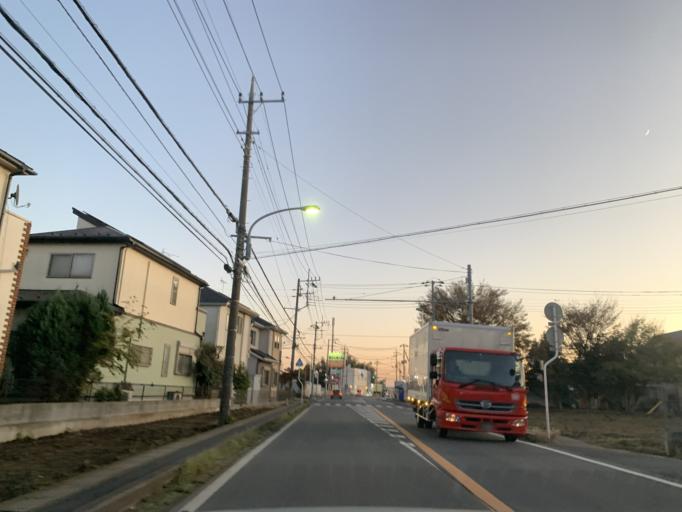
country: JP
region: Chiba
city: Nagareyama
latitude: 35.8981
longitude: 139.9024
